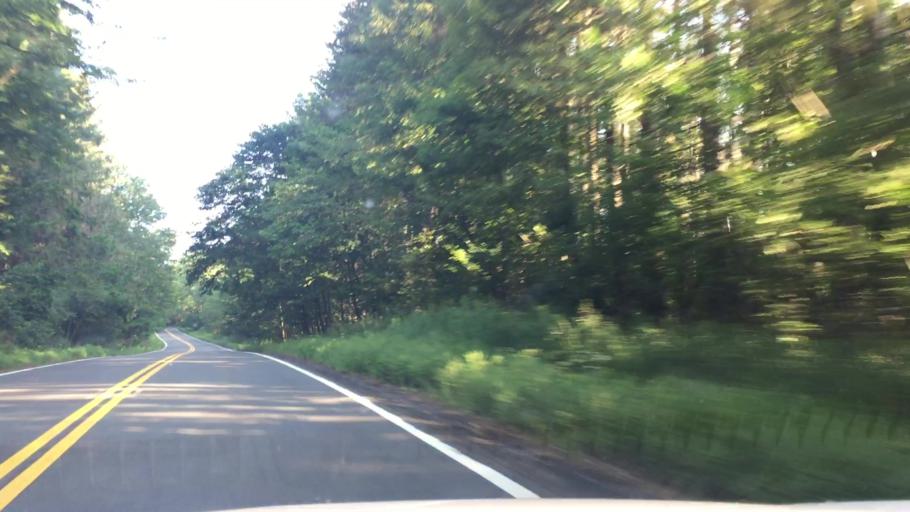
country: US
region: Massachusetts
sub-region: Berkshire County
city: Hinsdale
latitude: 42.3963
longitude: -73.1672
